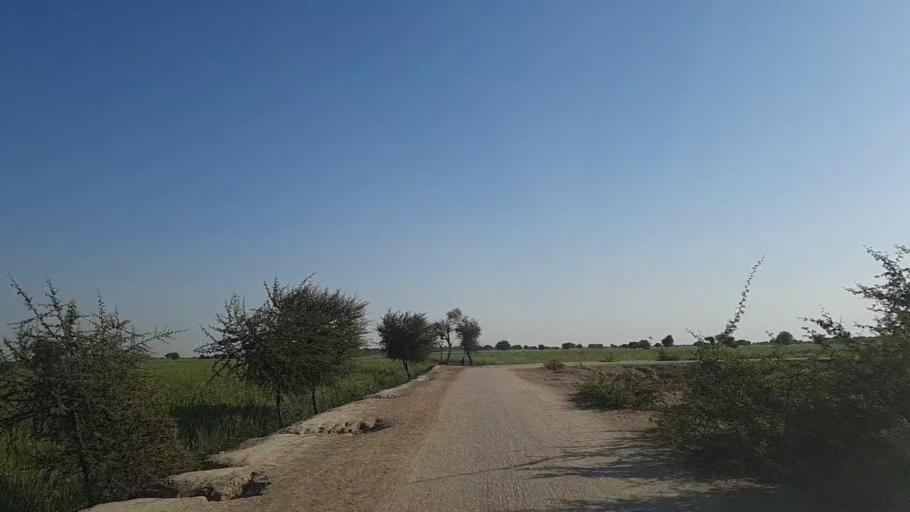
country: PK
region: Sindh
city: Naukot
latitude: 24.9427
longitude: 69.3364
